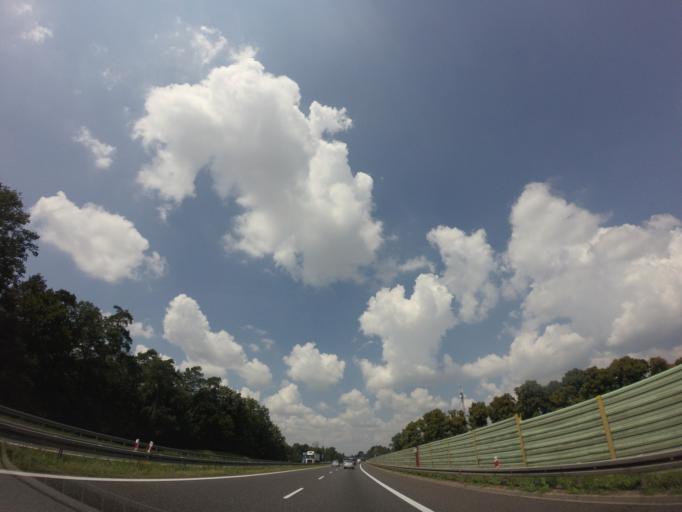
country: PL
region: Opole Voivodeship
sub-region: Powiat strzelecki
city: Ujazd
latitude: 50.4343
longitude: 18.3676
